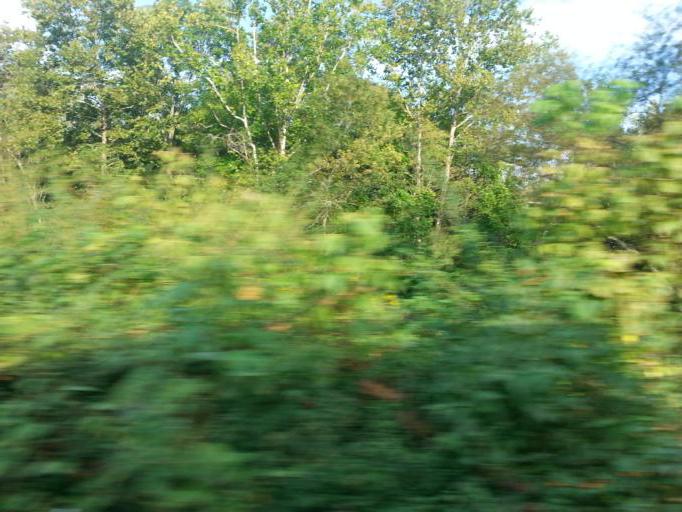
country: US
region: Tennessee
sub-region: Knox County
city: Knoxville
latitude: 35.8900
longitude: -83.8733
